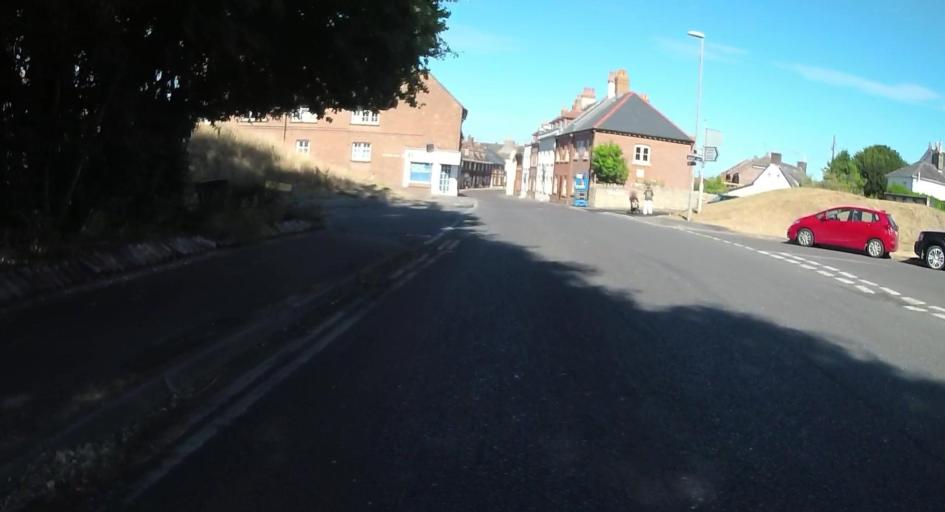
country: GB
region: England
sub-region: Dorset
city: Wareham
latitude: 50.6849
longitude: -2.1140
